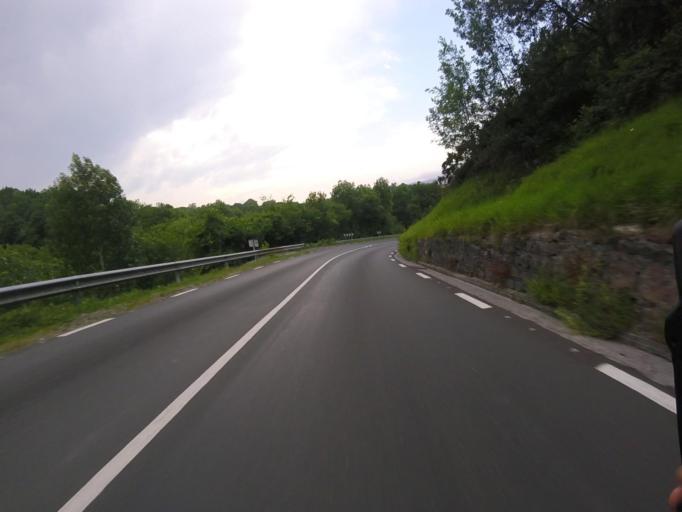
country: ES
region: Basque Country
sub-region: Provincia de Guipuzcoa
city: Errenteria
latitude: 43.3003
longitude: -1.9064
